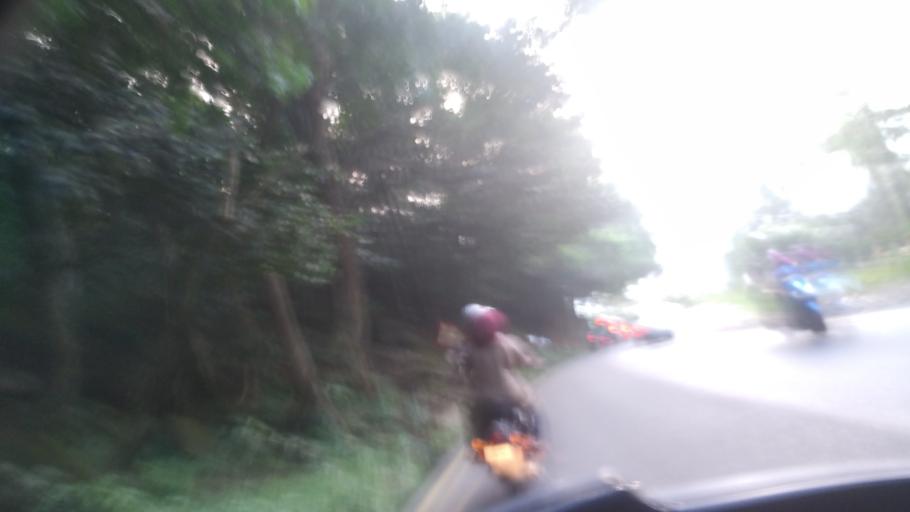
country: IN
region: Kerala
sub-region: Wayanad
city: Kalpetta
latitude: 11.5011
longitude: 76.0231
